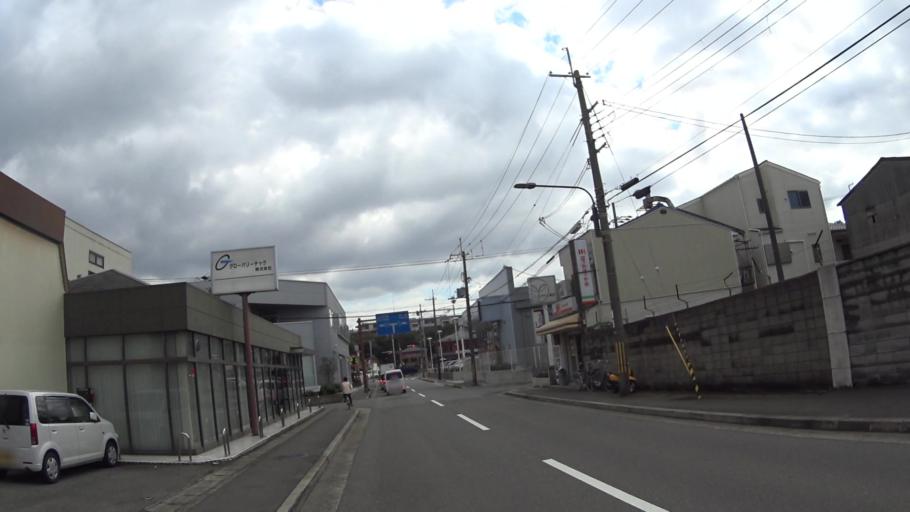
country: JP
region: Kyoto
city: Muko
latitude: 34.9594
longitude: 135.7154
